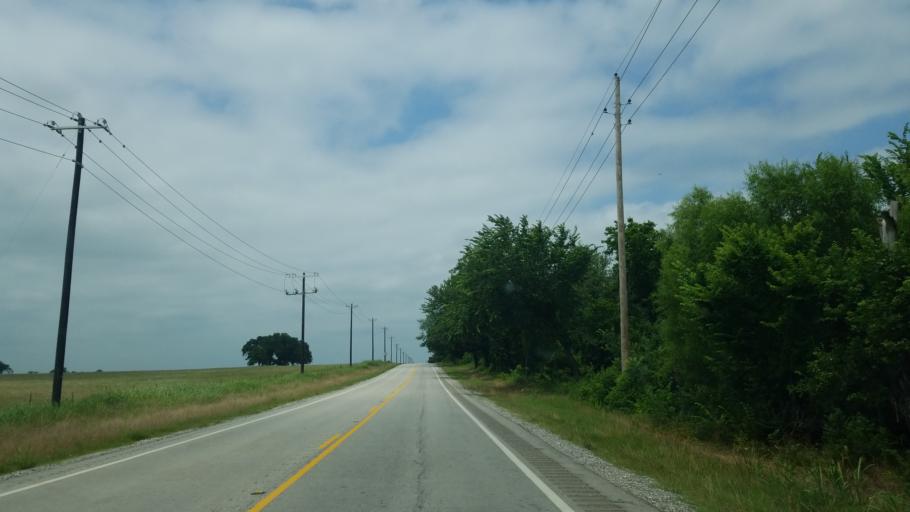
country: US
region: Texas
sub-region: Denton County
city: Aubrey
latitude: 33.3118
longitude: -96.9798
